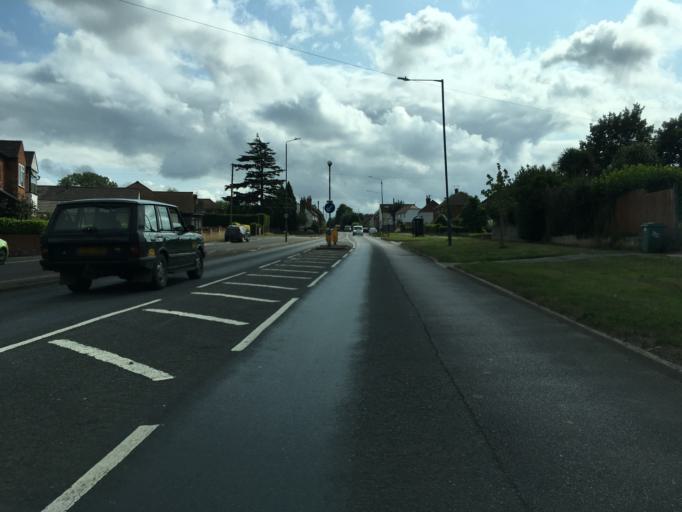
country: GB
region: England
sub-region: Kent
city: Maidstone
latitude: 51.2345
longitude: 0.5155
